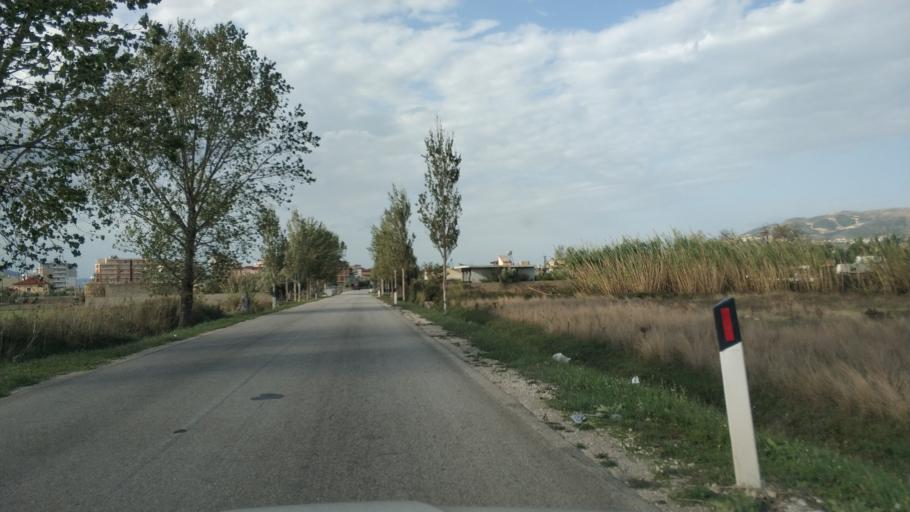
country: AL
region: Vlore
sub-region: Rrethi i Vlores
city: Orikum
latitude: 40.3245
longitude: 19.4799
